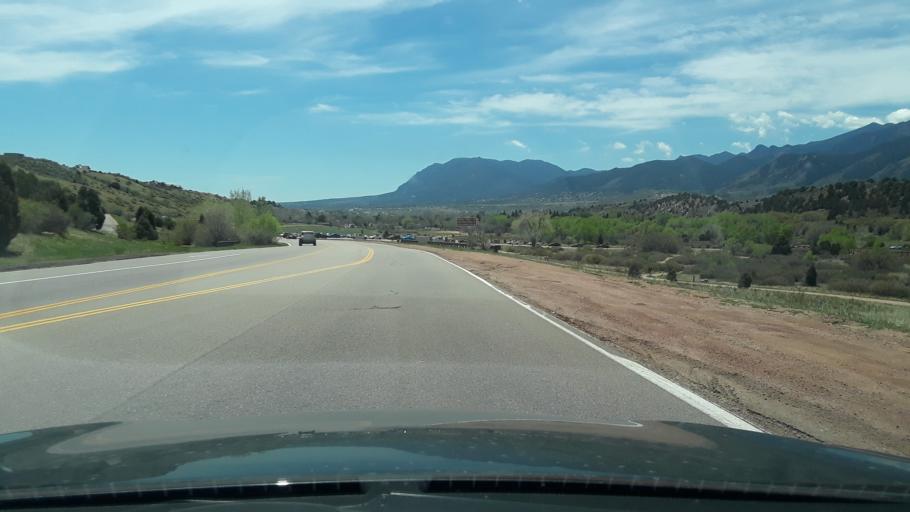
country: US
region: Colorado
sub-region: El Paso County
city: Manitou Springs
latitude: 38.8798
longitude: -104.8716
